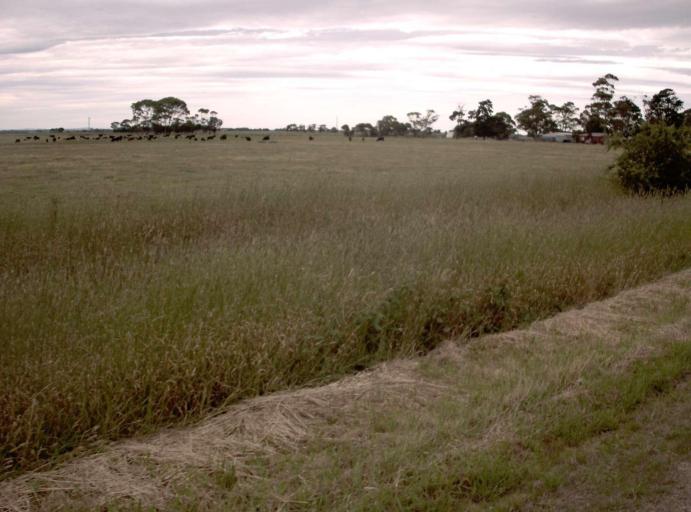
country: AU
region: Victoria
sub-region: Wellington
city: Sale
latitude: -38.0705
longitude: 147.0939
